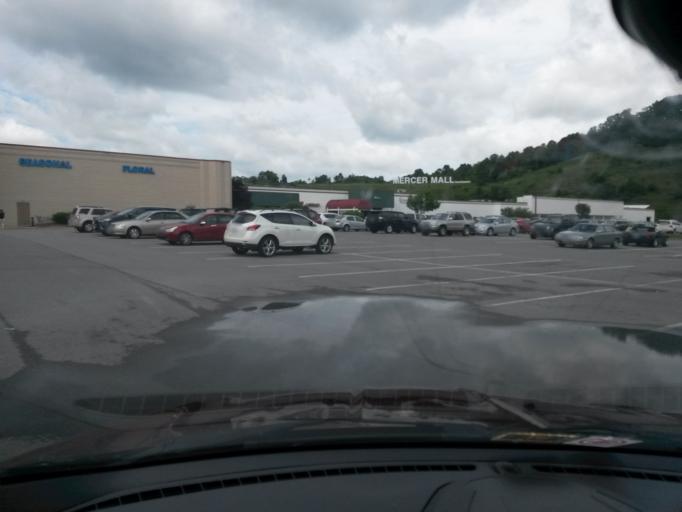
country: US
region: West Virginia
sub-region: Mercer County
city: Bluefield
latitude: 37.2981
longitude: -81.1664
